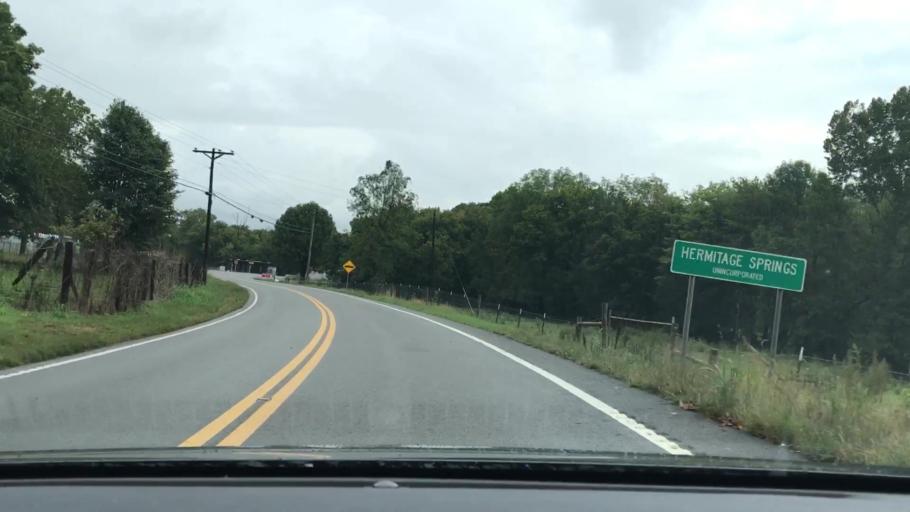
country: US
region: Tennessee
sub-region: Macon County
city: Red Boiling Springs
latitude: 36.5740
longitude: -85.7817
